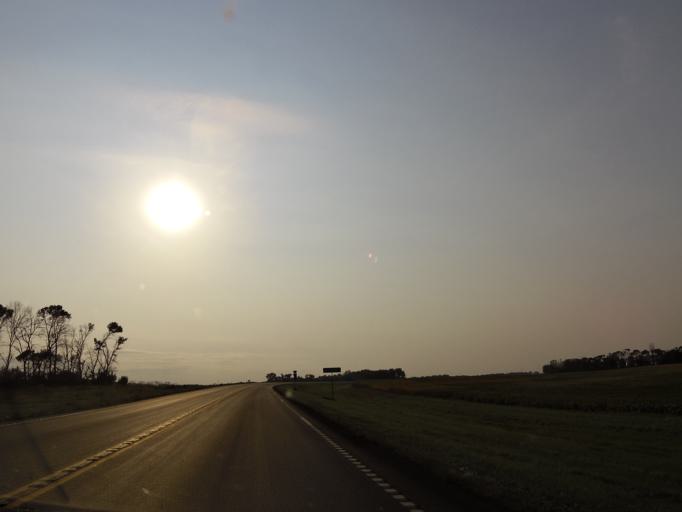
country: US
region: North Dakota
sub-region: Traill County
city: Mayville
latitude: 47.3528
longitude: -97.3171
